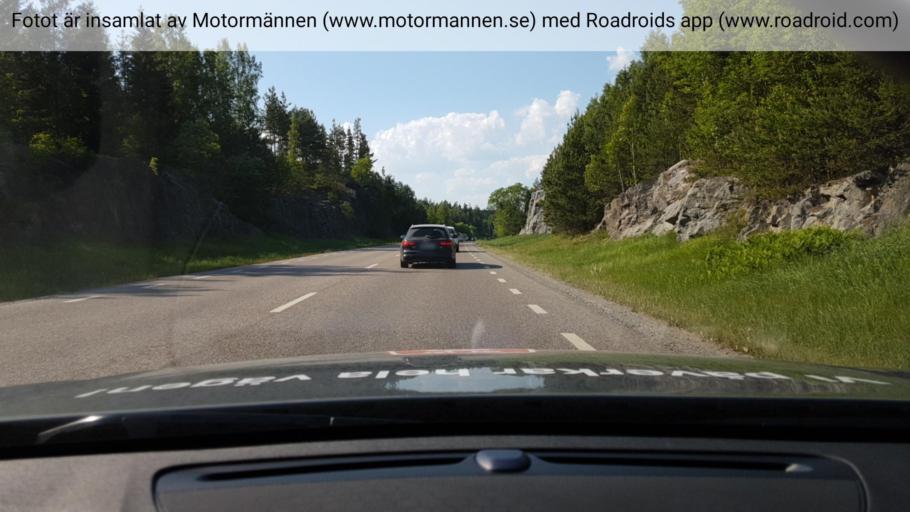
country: SE
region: Stockholm
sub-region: Varmdo Kommun
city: Gustavsberg
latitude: 59.2911
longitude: 18.3956
